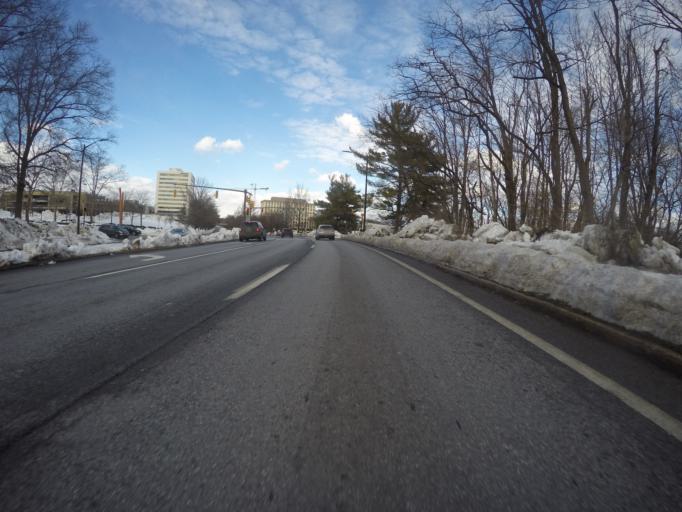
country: US
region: Maryland
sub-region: Howard County
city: Columbia
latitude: 39.2122
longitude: -76.8578
